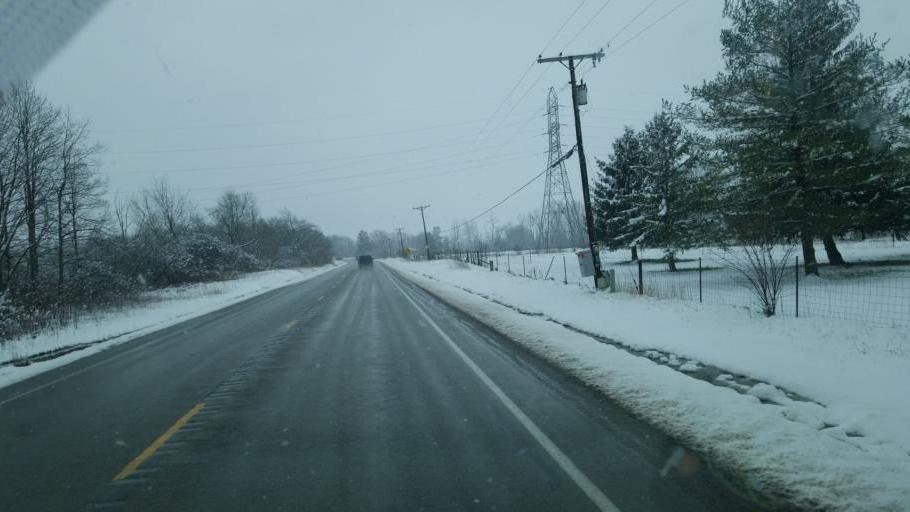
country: US
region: Indiana
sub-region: Delaware County
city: Muncie
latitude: 40.1490
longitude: -85.3439
